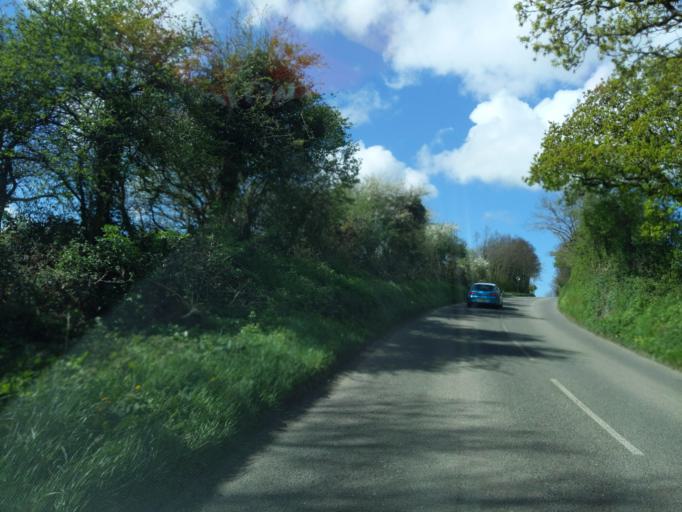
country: GB
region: England
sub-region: Cornwall
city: Wadebridge
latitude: 50.5281
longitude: -4.8336
